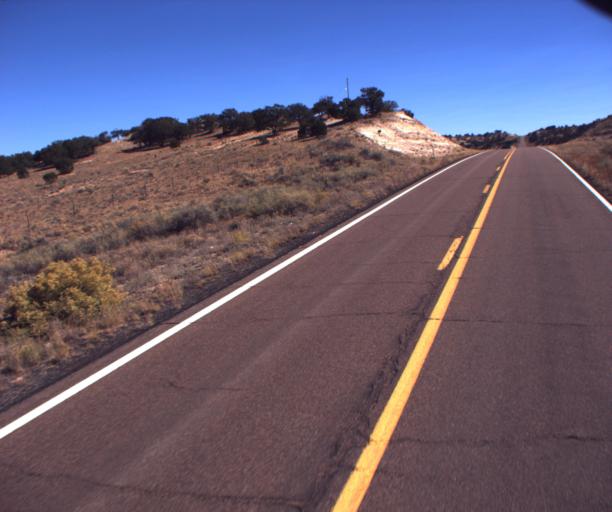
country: US
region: Arizona
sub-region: Navajo County
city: First Mesa
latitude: 35.7637
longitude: -109.9773
